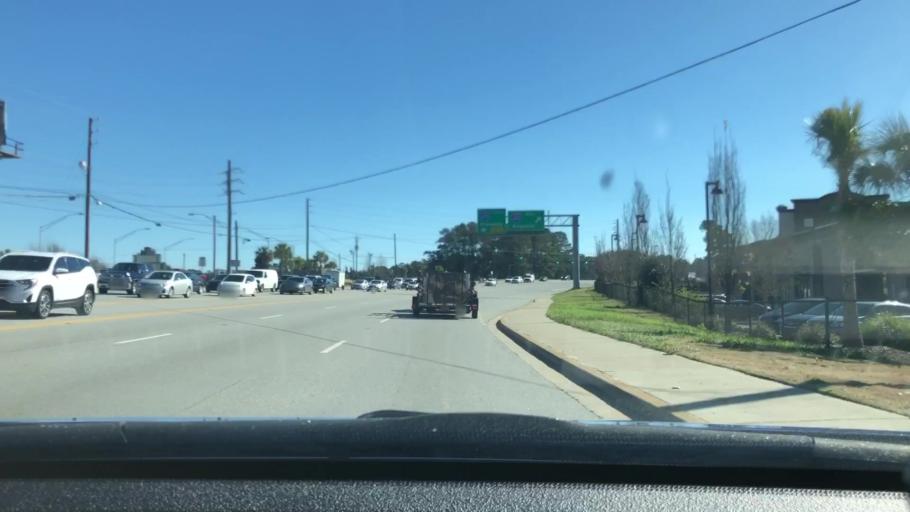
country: US
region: South Carolina
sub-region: Lexington County
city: Oak Grove
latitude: 34.0135
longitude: -81.1519
